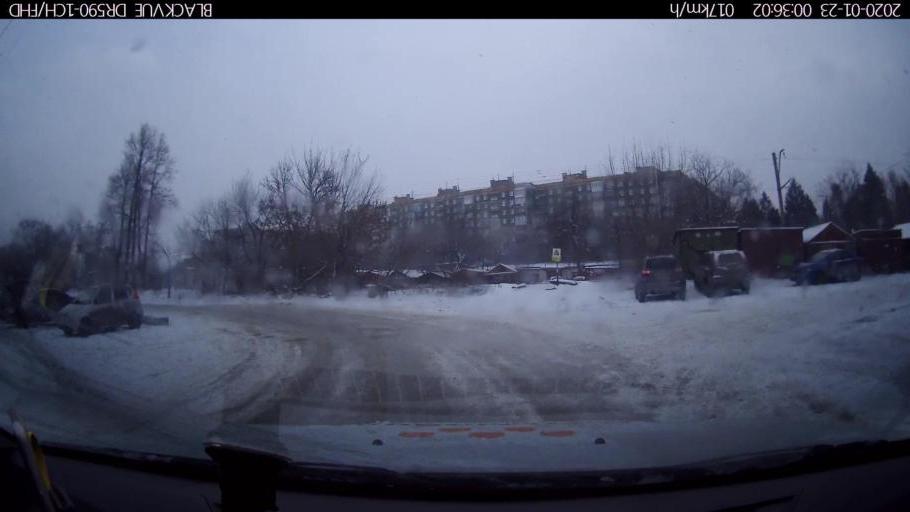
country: RU
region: Nizjnij Novgorod
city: Neklyudovo
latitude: 56.3559
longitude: 43.8544
